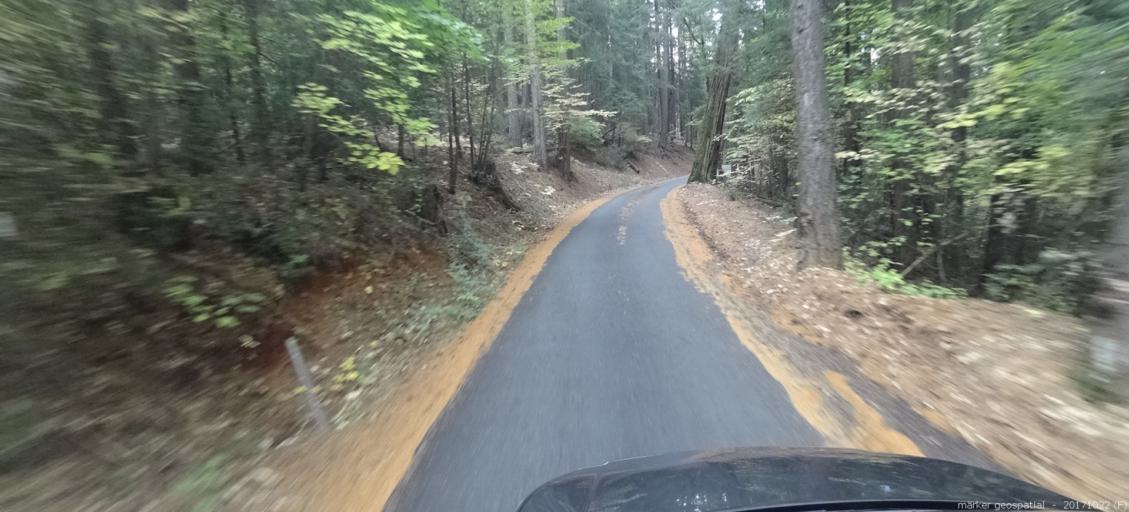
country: US
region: California
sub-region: Siskiyou County
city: Dunsmuir
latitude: 41.1601
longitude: -122.2903
